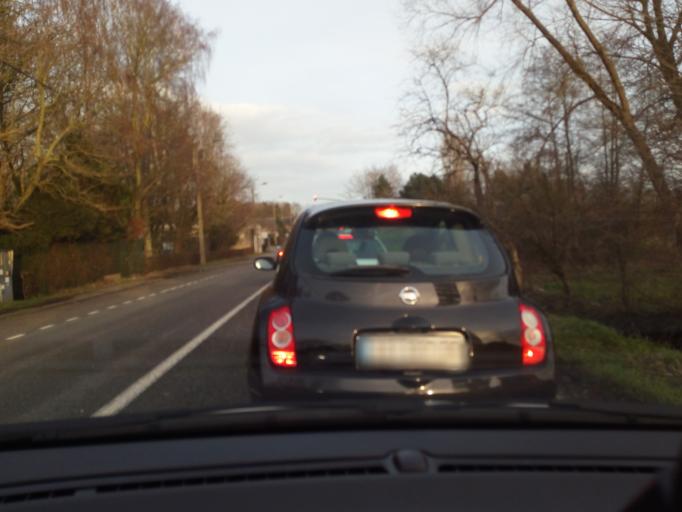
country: FR
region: Nord-Pas-de-Calais
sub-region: Departement du Nord
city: Louvroil
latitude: 50.2574
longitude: 3.9568
